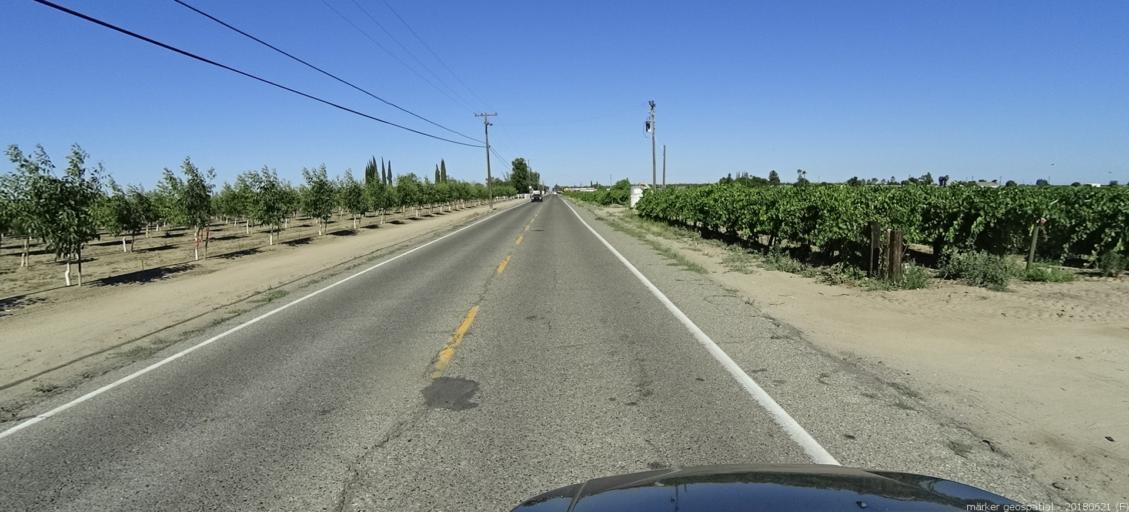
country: US
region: California
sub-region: Fresno County
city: Biola
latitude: 36.8513
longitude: -120.0509
